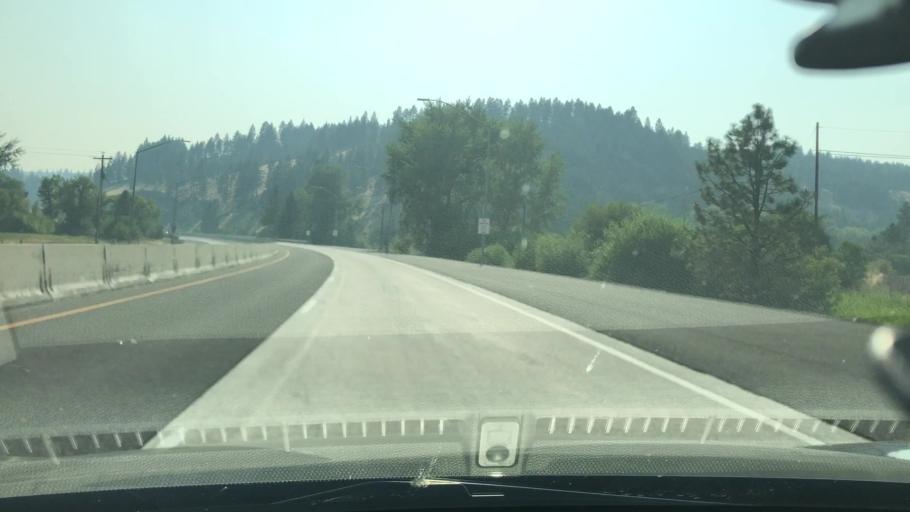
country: US
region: Oregon
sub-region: Union County
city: La Grande
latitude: 45.3482
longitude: -118.2193
